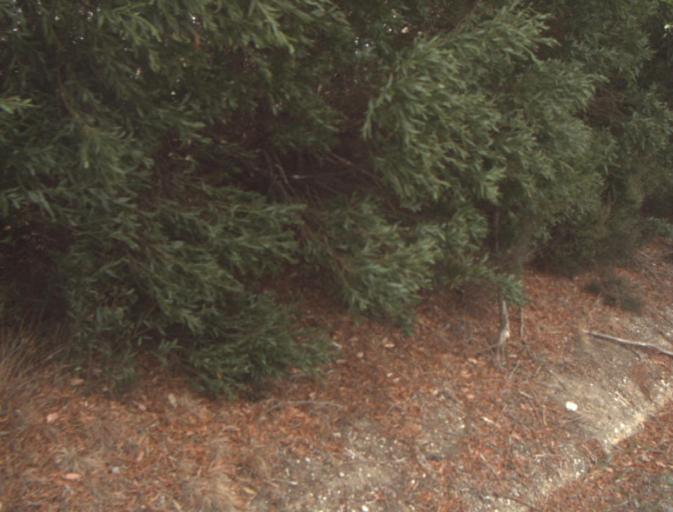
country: AU
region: Tasmania
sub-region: Launceston
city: Mayfield
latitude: -41.2060
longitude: 147.2150
